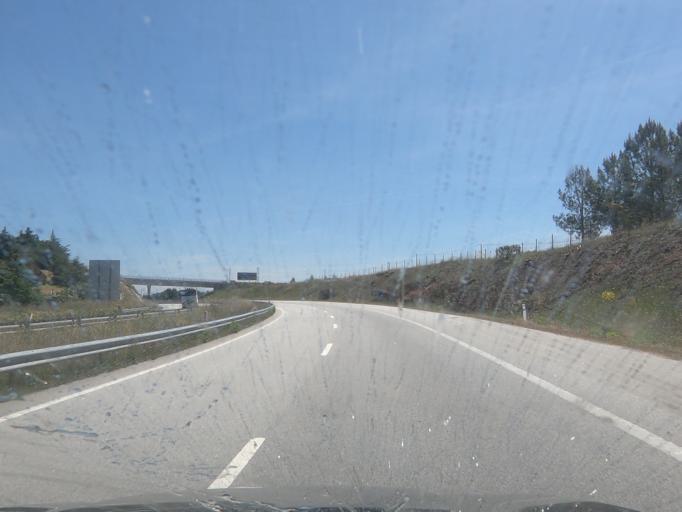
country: PT
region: Guarda
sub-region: Guarda
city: Sequeira
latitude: 40.5621
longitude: -7.2269
